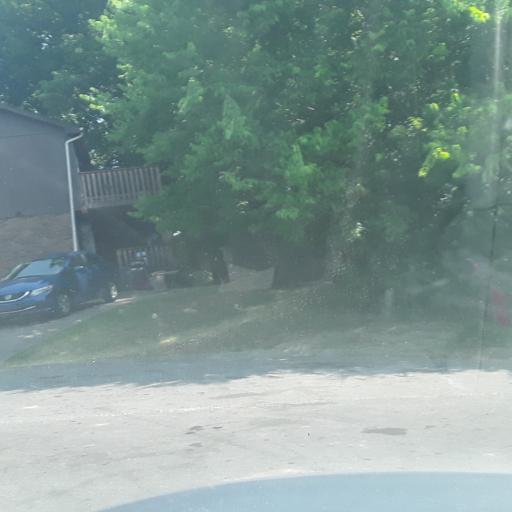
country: US
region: Tennessee
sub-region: Williamson County
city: Brentwood Estates
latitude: 36.0382
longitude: -86.7045
